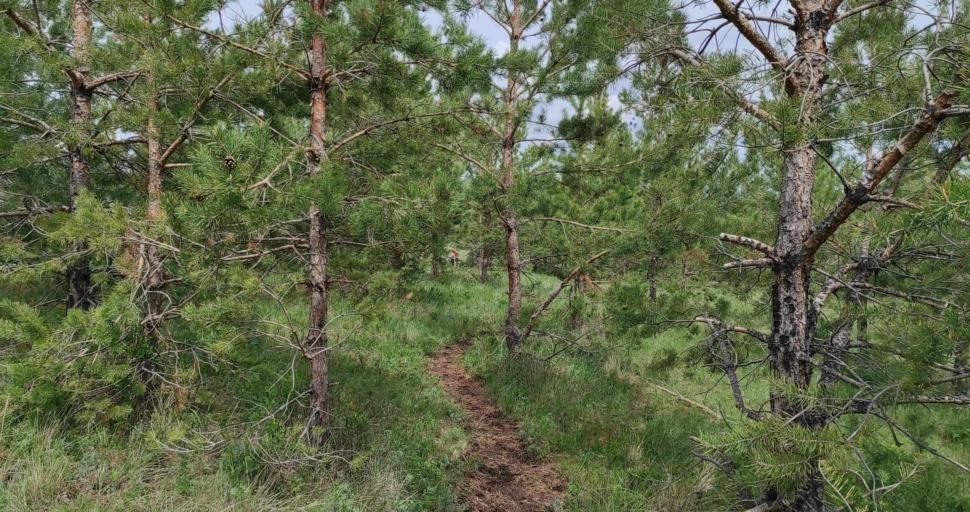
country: RU
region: Bashkortostan
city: Sibay
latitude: 52.6895
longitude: 58.5401
